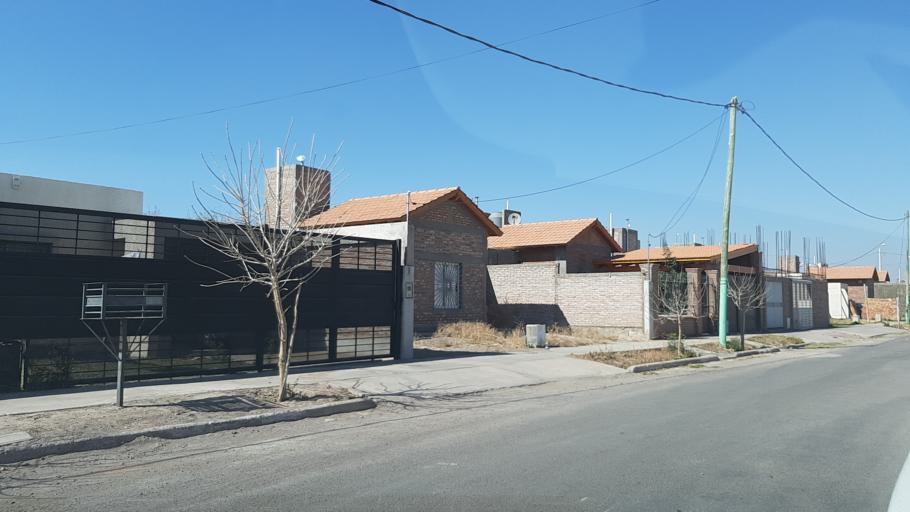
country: AR
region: San Juan
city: San Juan
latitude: -31.5223
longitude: -68.5894
